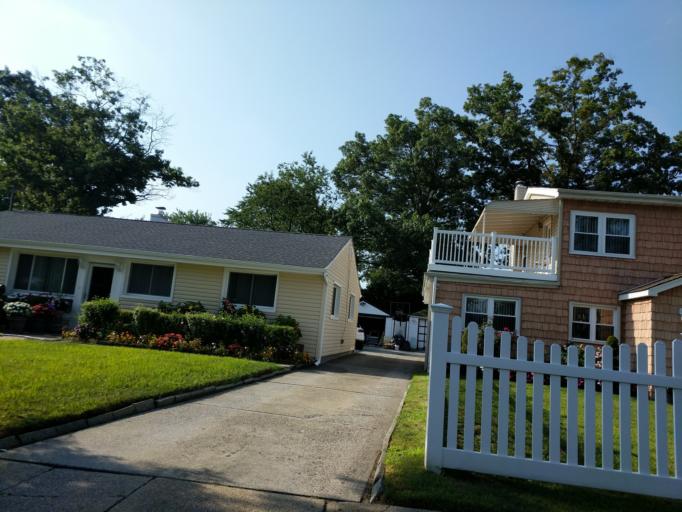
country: US
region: New York
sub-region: Nassau County
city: Valley Stream
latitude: 40.6543
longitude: -73.7048
